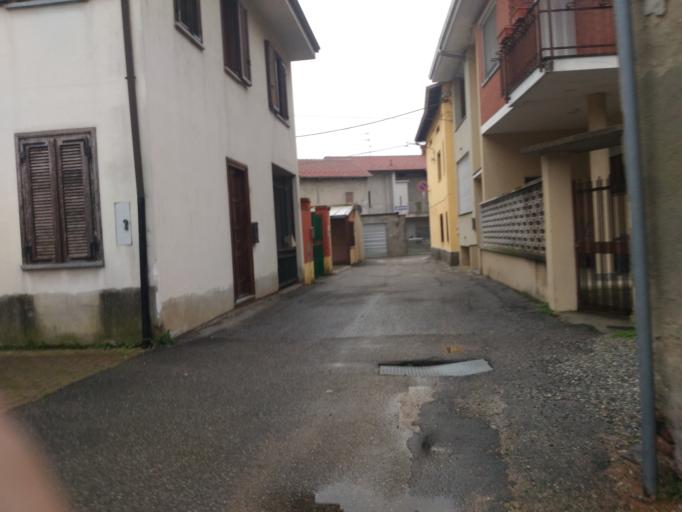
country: IT
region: Piedmont
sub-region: Provincia di Vercelli
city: Cigliano
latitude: 45.3086
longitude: 8.0219
